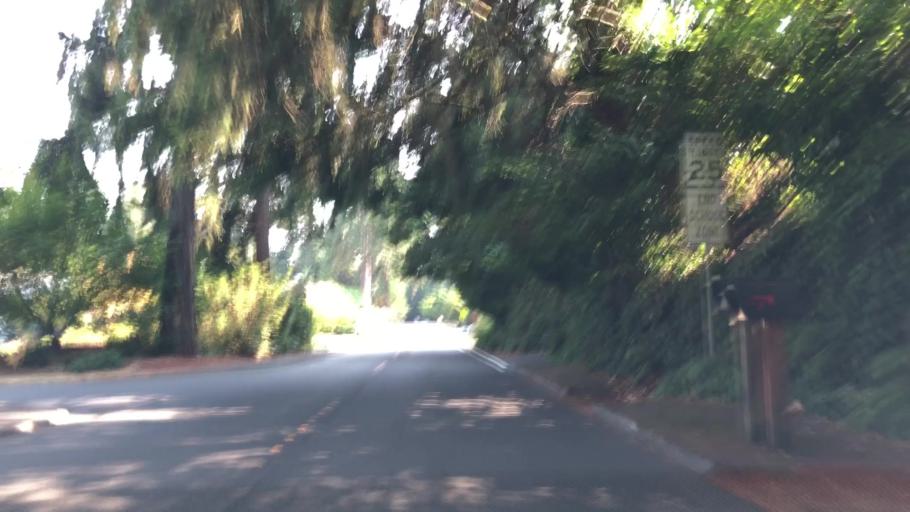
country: US
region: Washington
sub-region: King County
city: Bellevue
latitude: 47.5892
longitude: -122.2028
